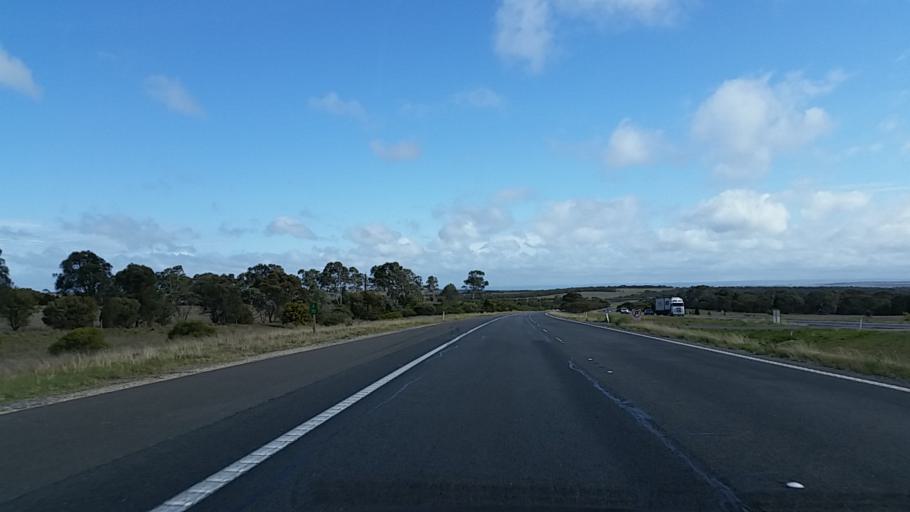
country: AU
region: South Australia
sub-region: Murray Bridge
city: Murray Bridge
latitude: -35.1514
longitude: 139.2065
